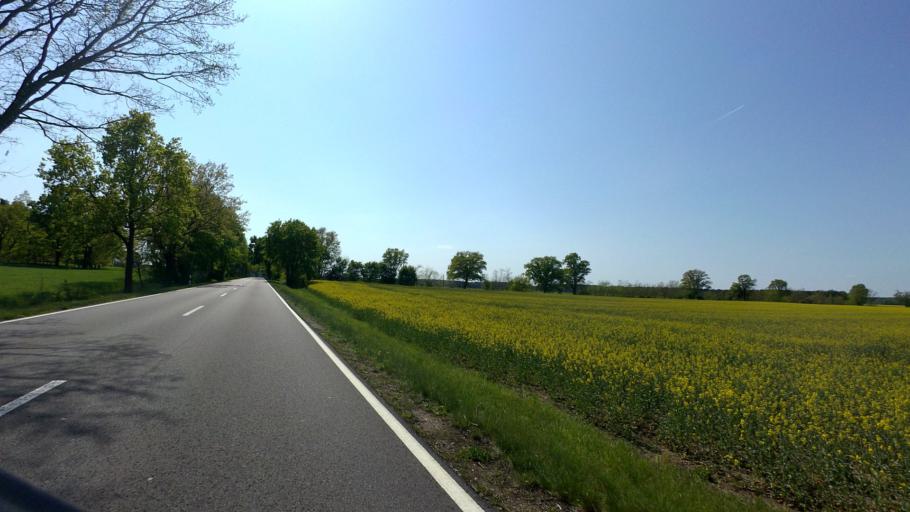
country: DE
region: Brandenburg
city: Neu Zauche
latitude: 52.0166
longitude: 14.0694
